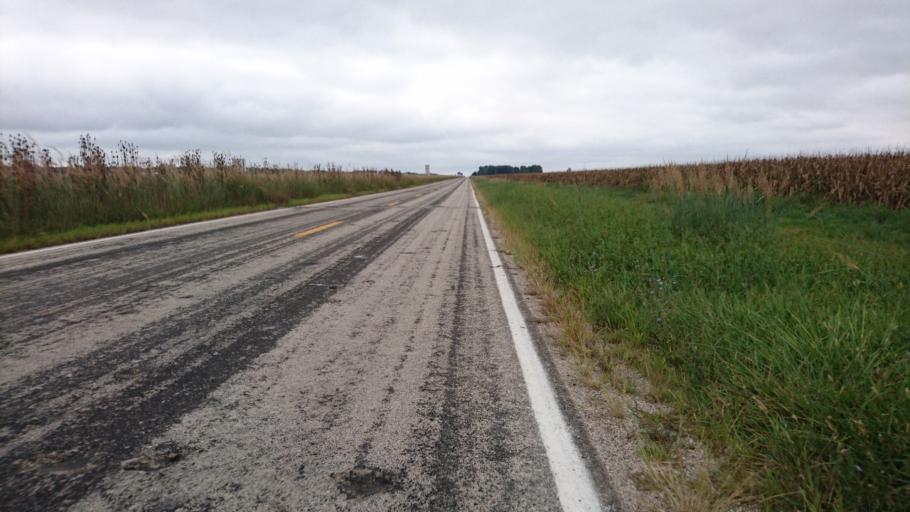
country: US
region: Illinois
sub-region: Montgomery County
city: Raymond
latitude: 39.3132
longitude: -89.6430
